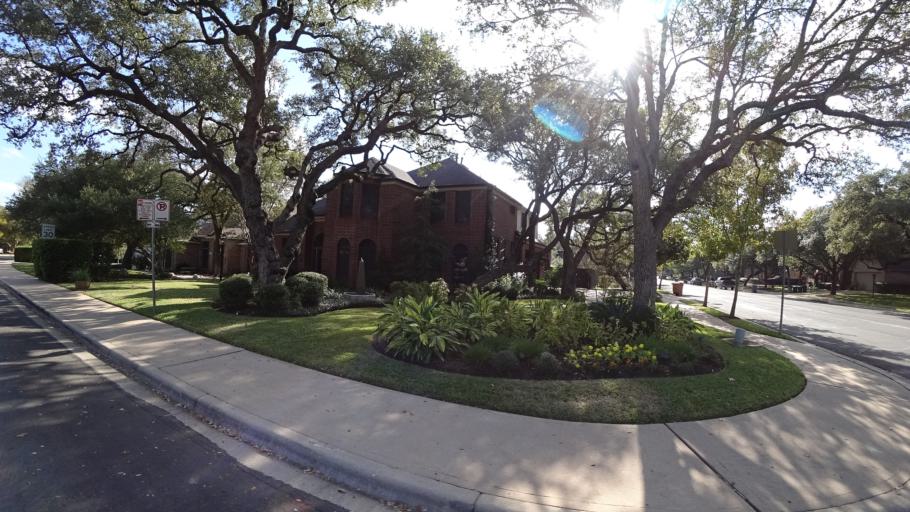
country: US
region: Texas
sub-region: Travis County
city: Shady Hollow
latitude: 30.1827
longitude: -97.8573
